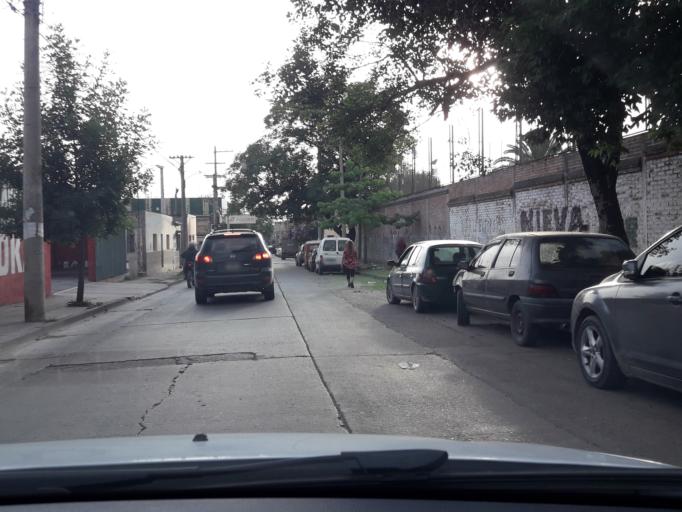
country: AR
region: Jujuy
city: San Salvador de Jujuy
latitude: -24.1908
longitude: -65.3087
